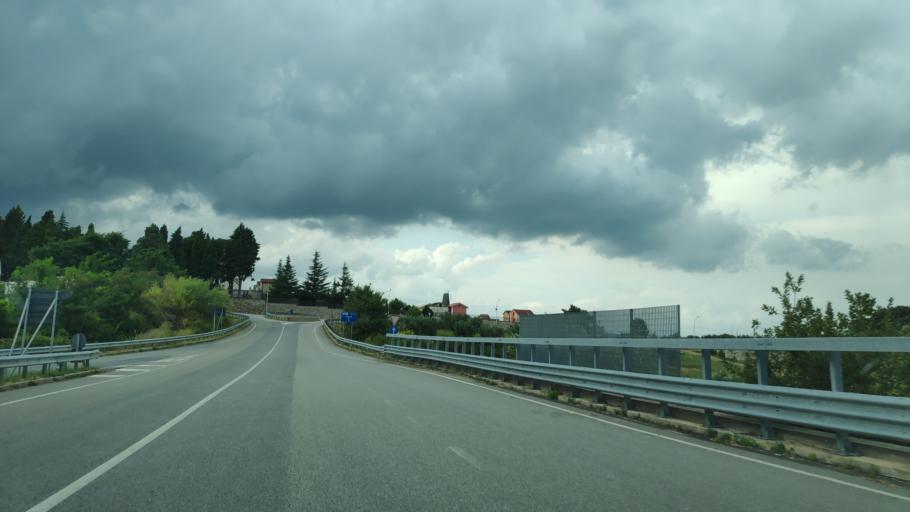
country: IT
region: Calabria
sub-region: Provincia di Catanzaro
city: Argusto
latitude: 38.6811
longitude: 16.4248
